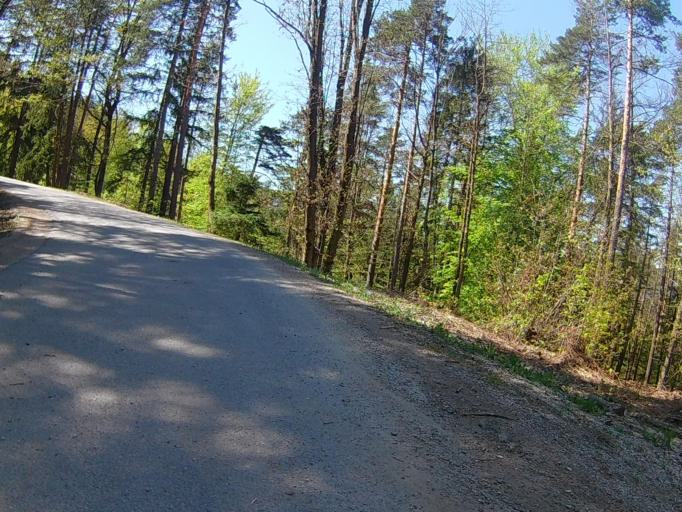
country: SI
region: Ruse
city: Ruse
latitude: 46.5343
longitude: 15.5147
